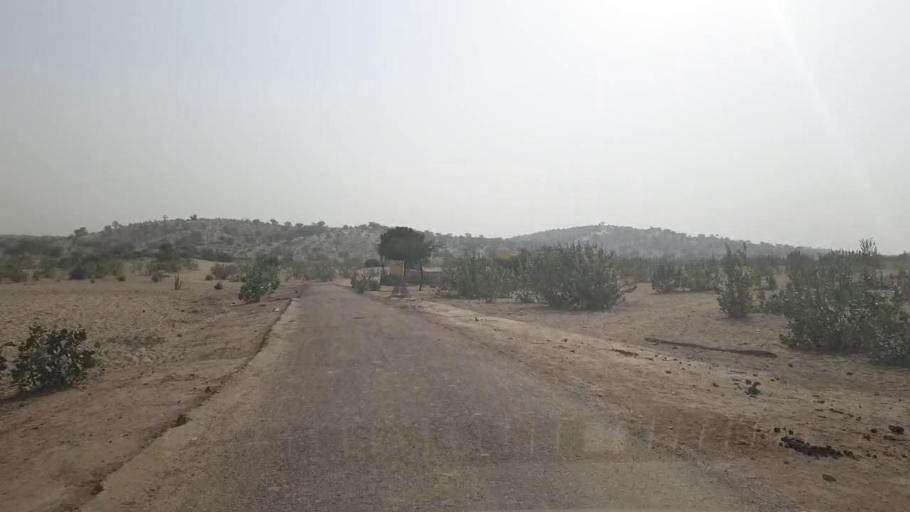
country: PK
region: Sindh
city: Chor
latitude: 25.6204
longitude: 69.9235
